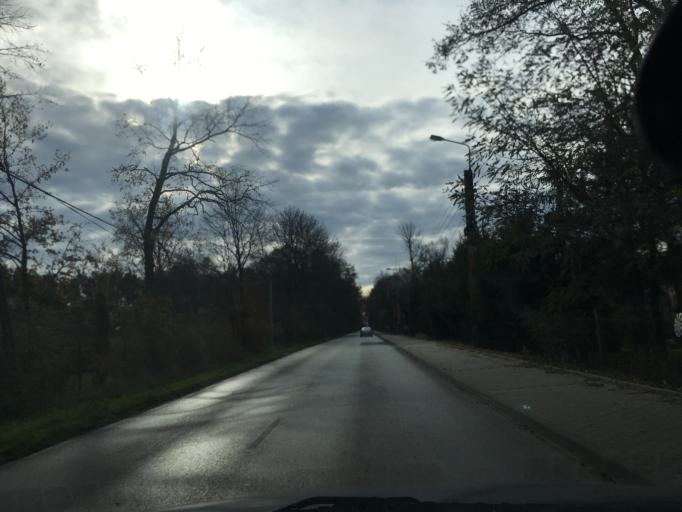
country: PL
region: Masovian Voivodeship
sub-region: Powiat piaseczynski
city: Lesznowola
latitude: 52.0244
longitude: 20.9567
